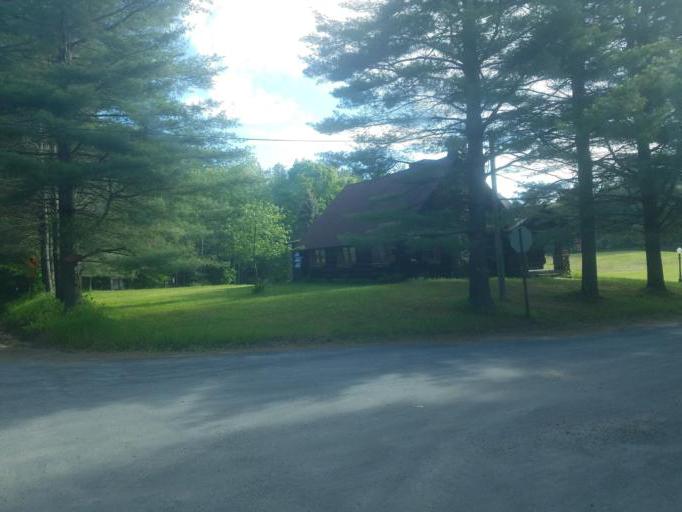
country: US
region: New York
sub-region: Herkimer County
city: Dolgeville
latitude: 43.3602
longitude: -74.9202
